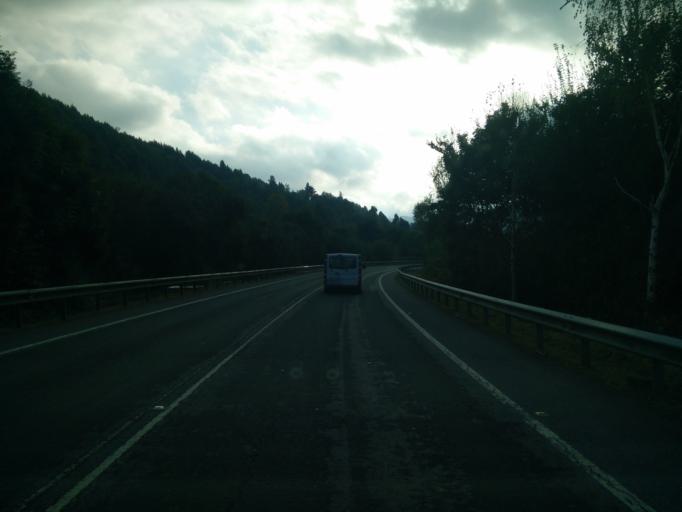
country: ES
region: Basque Country
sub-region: Bizkaia
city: Berriatua
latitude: 43.3188
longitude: -2.4457
